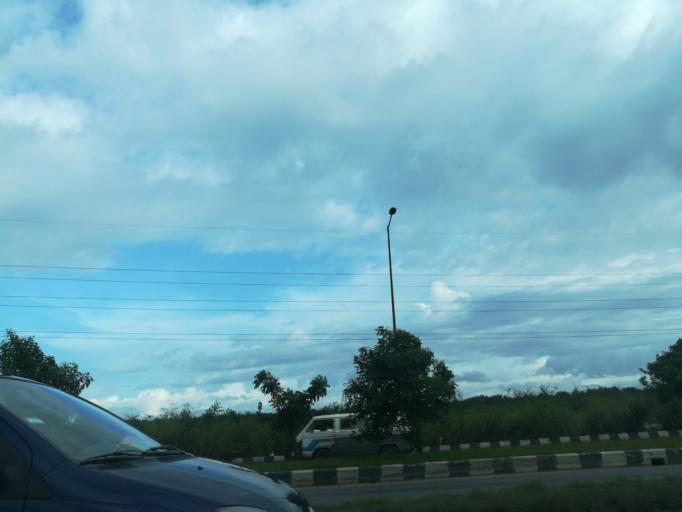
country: NG
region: Lagos
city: Ebute Ikorodu
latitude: 6.6210
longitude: 3.4512
